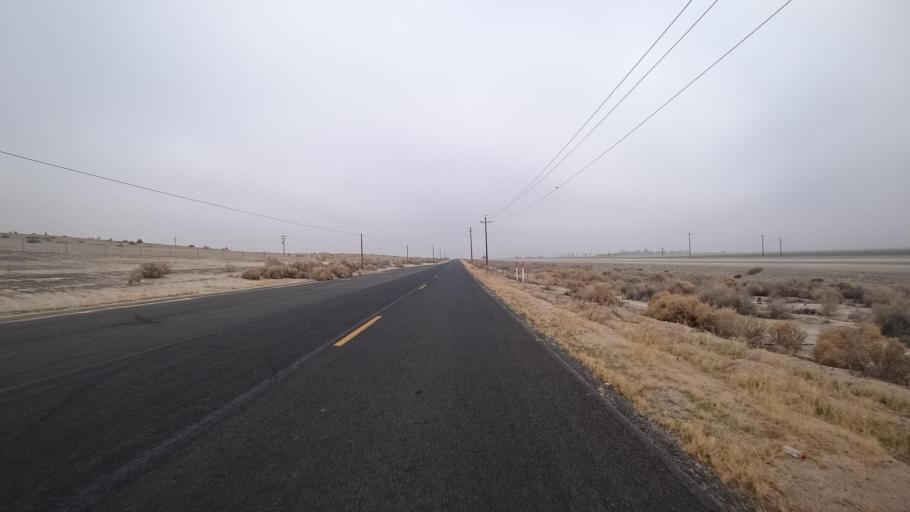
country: US
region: California
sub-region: Kern County
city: Ford City
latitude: 35.2383
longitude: -119.3164
